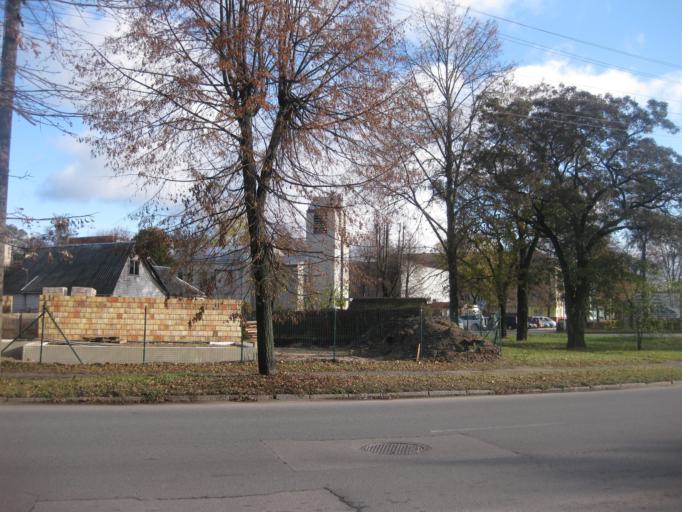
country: LT
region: Kauno apskritis
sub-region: Kaunas
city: Silainiai
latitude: 54.9135
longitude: 23.8883
